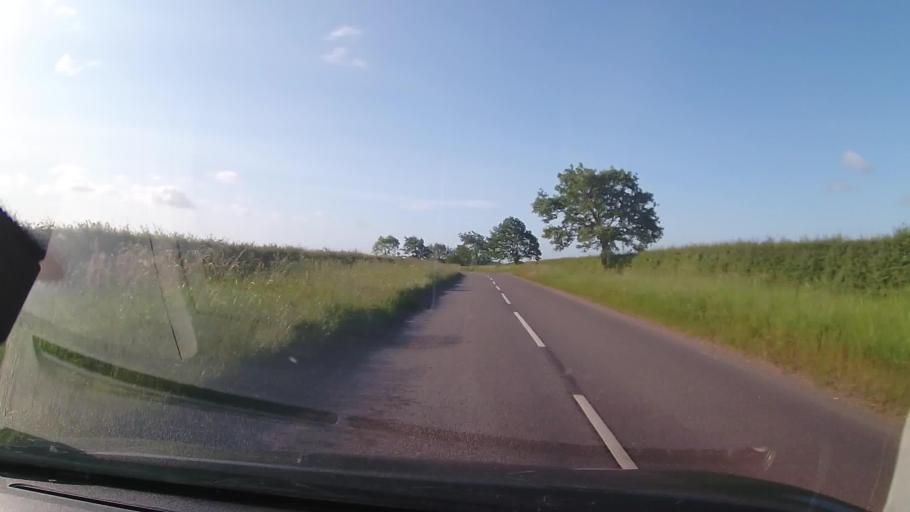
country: GB
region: England
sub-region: Shropshire
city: Shawbury
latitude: 52.8109
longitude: -2.6605
